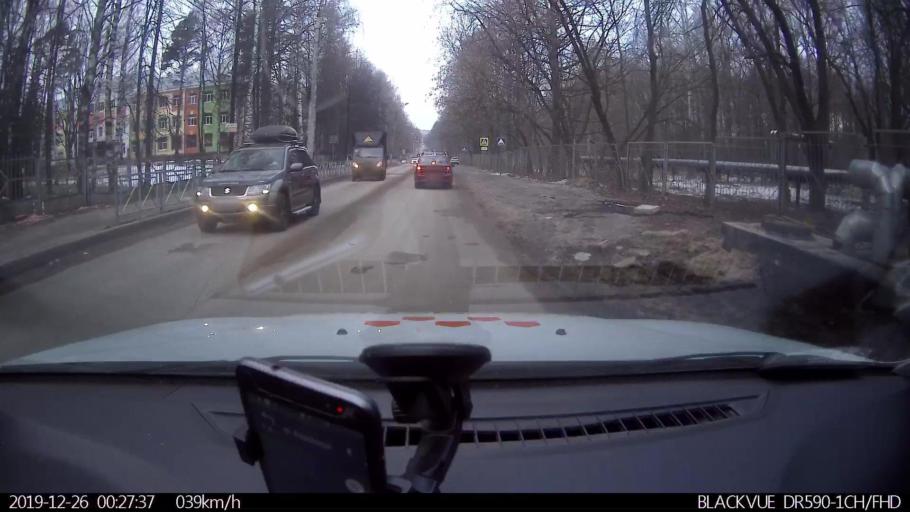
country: RU
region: Nizjnij Novgorod
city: Nizhniy Novgorod
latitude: 56.2652
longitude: 43.9977
